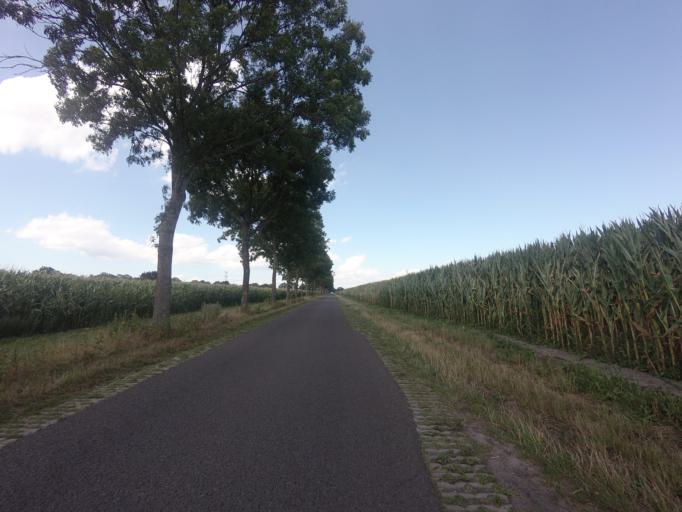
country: NL
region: Overijssel
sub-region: Gemeente Twenterand
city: Den Ham
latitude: 52.5754
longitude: 6.4508
